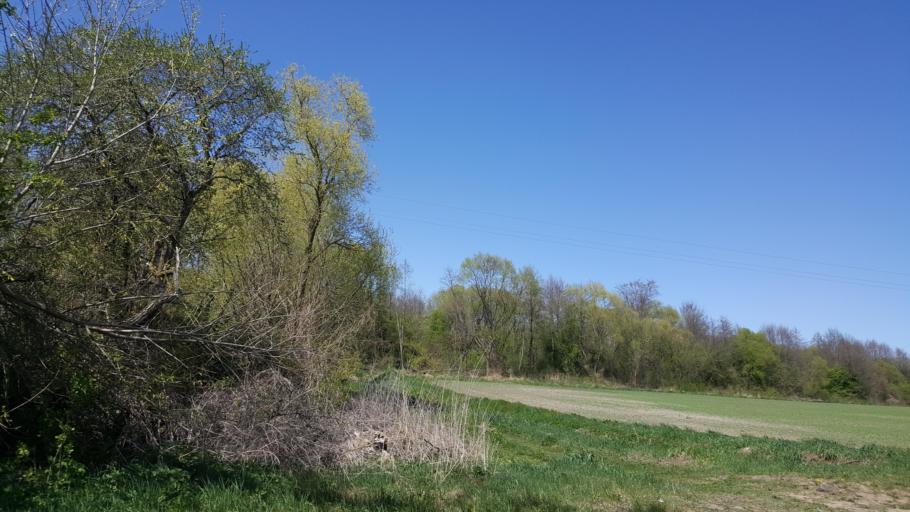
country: BY
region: Brest
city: Charnawchytsy
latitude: 52.3270
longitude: 23.6136
